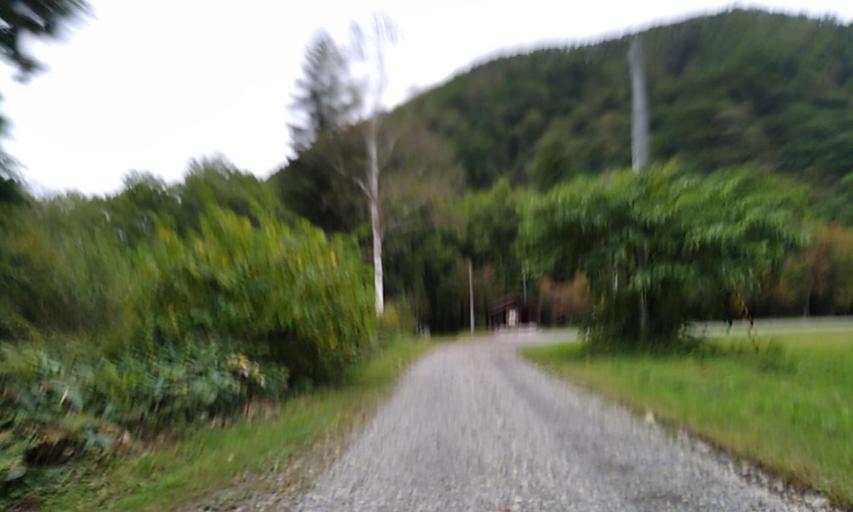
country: JP
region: Hokkaido
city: Obihiro
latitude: 42.6687
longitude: 143.0338
